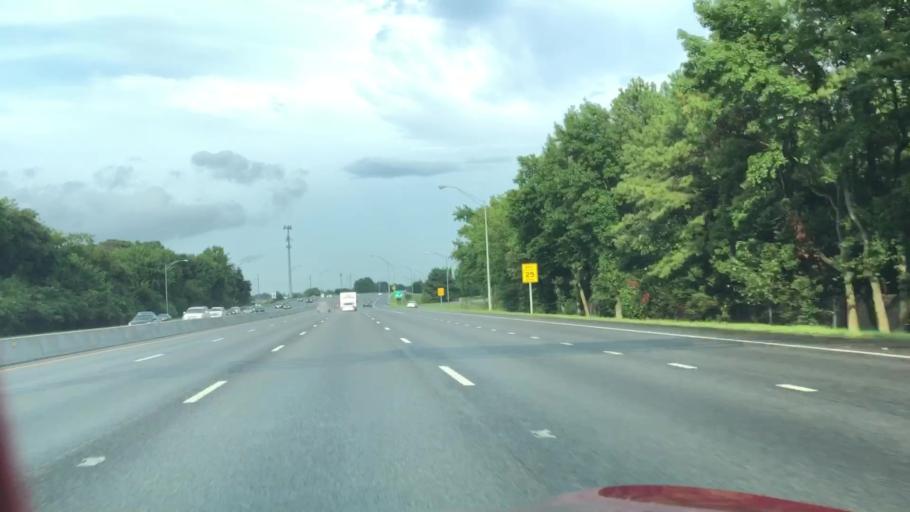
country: US
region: Virginia
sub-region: City of Virginia Beach
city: Virginia Beach
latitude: 36.8377
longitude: -76.1031
